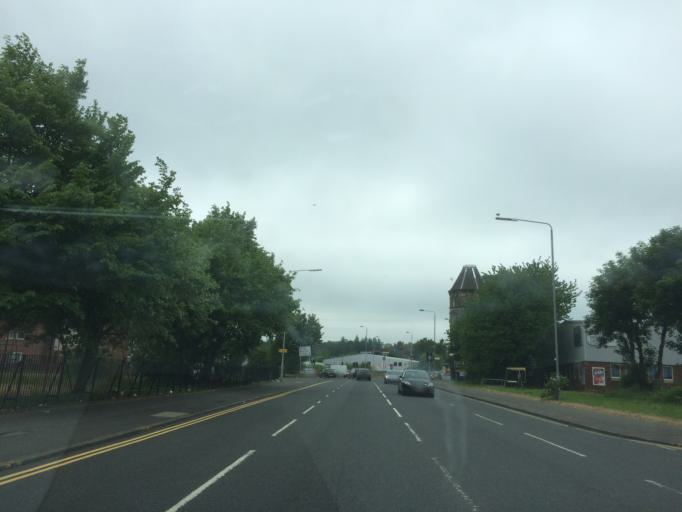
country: GB
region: Scotland
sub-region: Glasgow City
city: Glasgow
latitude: 55.8733
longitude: -4.2613
